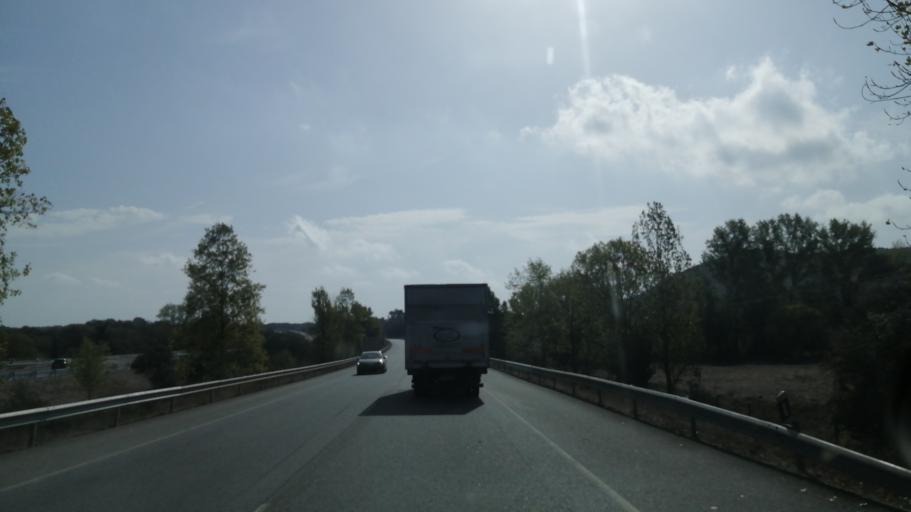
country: PT
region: Evora
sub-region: Montemor-O-Novo
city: Montemor-o-Novo
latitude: 38.6324
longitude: -8.1199
